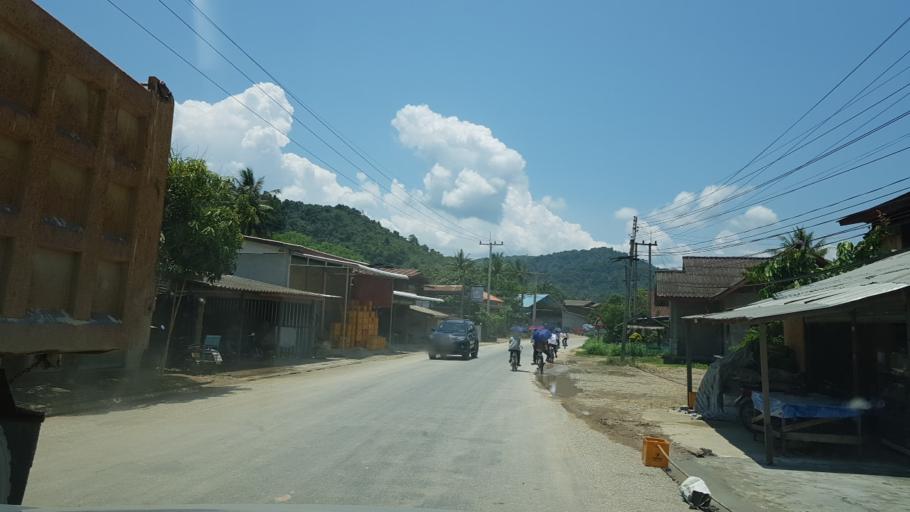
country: LA
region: Vientiane
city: Muang Kasi
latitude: 19.2330
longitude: 102.2526
